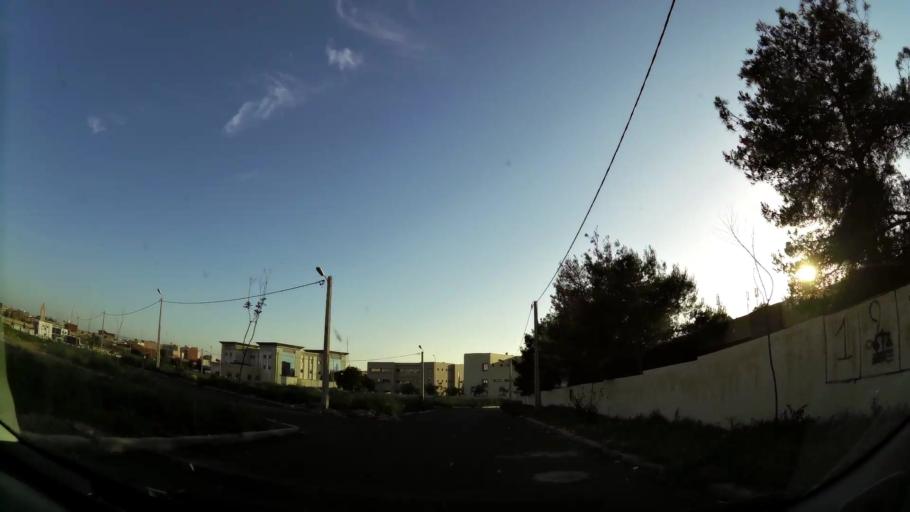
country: MA
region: Oriental
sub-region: Oujda-Angad
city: Oujda
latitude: 34.6994
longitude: -1.9173
